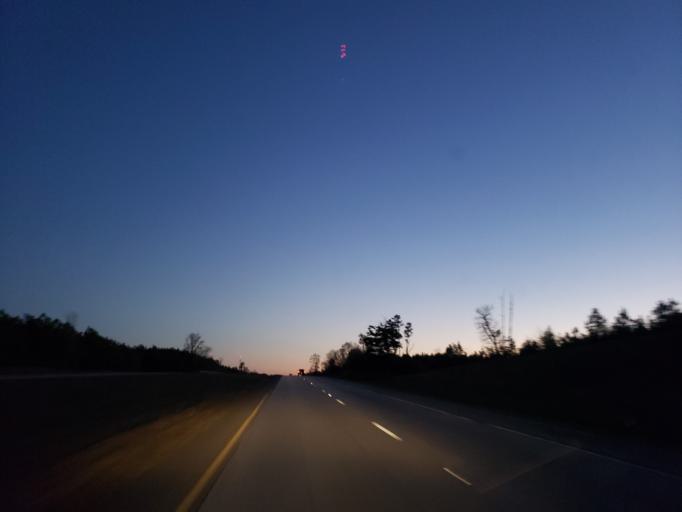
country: US
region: Mississippi
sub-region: Forrest County
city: Rawls Springs
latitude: 31.4469
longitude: -89.3213
